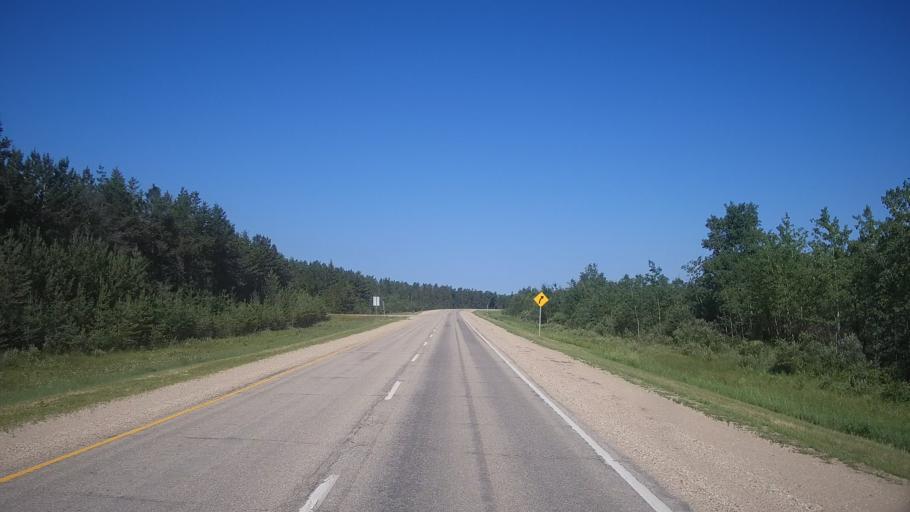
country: CA
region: Manitoba
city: La Broquerie
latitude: 49.6494
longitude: -95.9672
